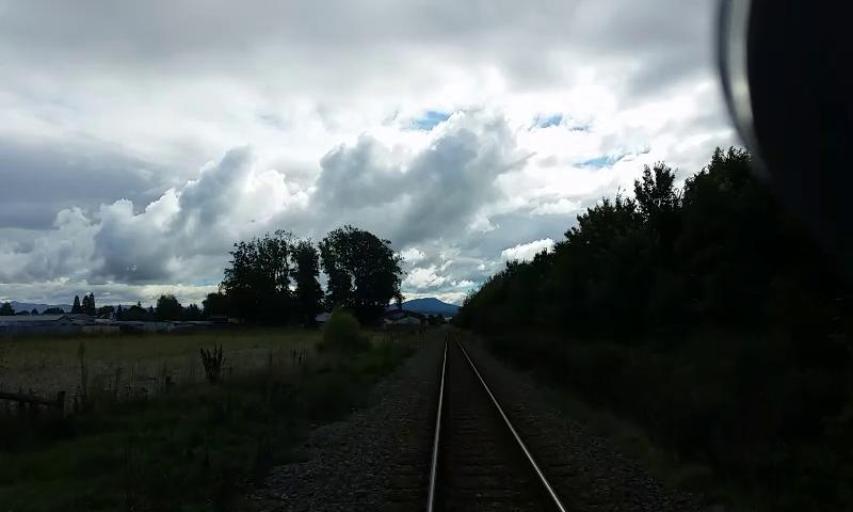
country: NZ
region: Canterbury
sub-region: Waimakariri District
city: Woodend
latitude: -43.3163
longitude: 172.6015
